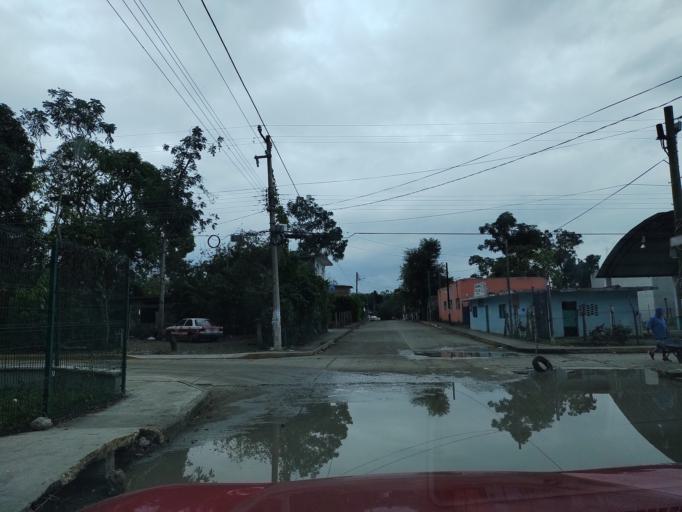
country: MX
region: Veracruz
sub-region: Papantla
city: El Chote
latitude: 20.4305
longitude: -97.3815
